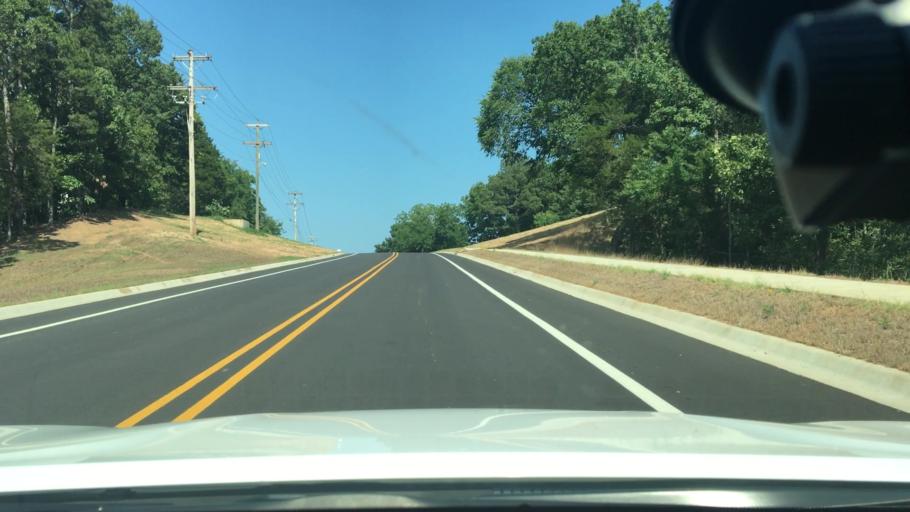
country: US
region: Arkansas
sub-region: Johnson County
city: Clarksville
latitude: 35.4620
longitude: -93.4958
